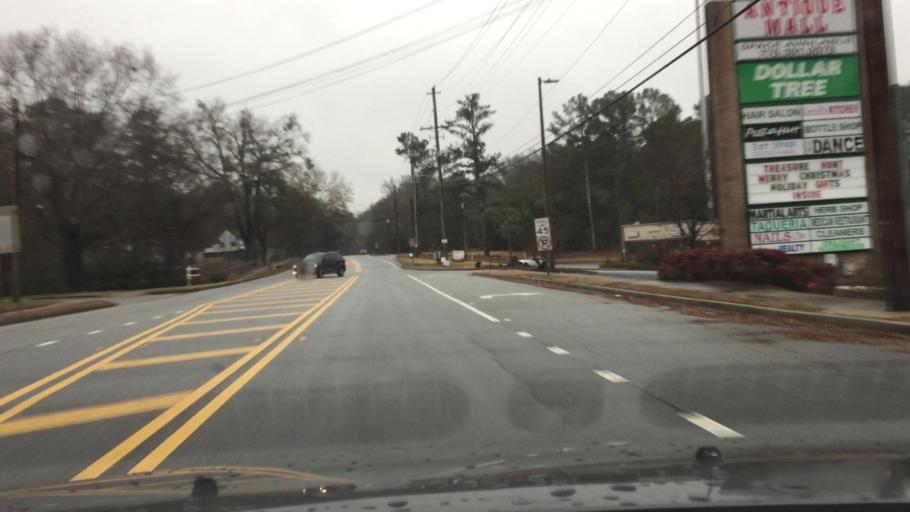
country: US
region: Georgia
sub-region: Cobb County
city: Powder Springs
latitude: 33.8741
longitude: -84.6762
